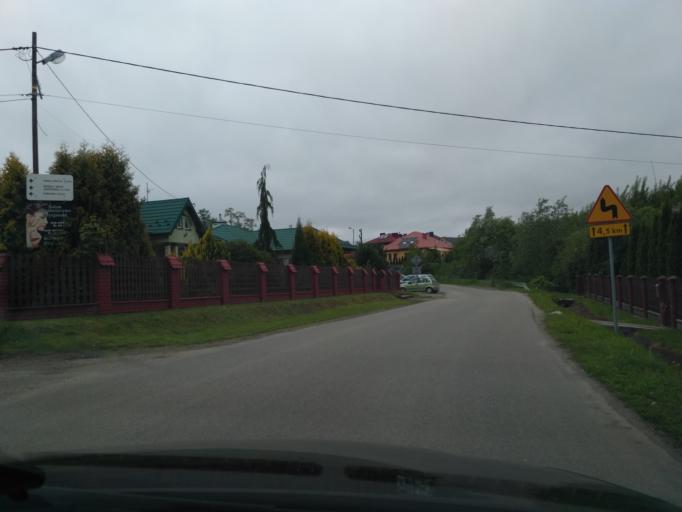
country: PL
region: Subcarpathian Voivodeship
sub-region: Powiat jasielski
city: Brzyska
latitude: 49.8218
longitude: 21.3886
